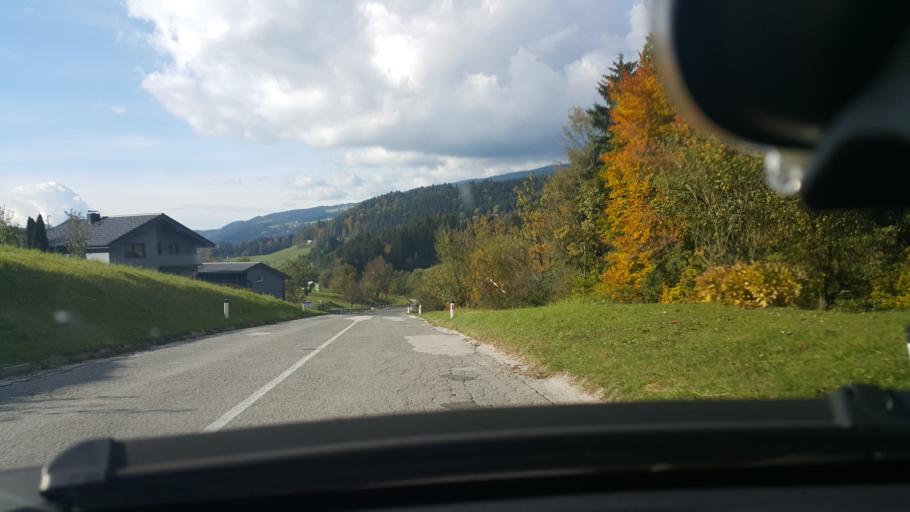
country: SI
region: Vitanje
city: Vitanje
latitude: 46.3795
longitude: 15.3301
